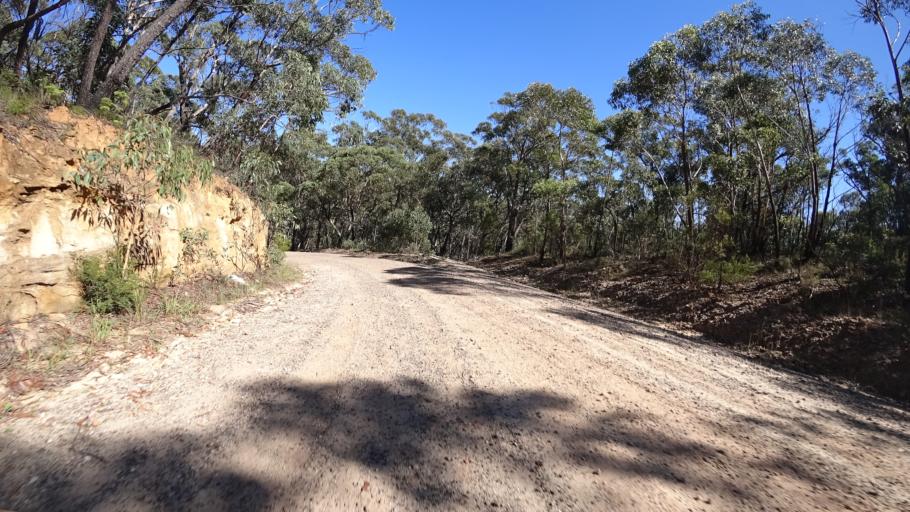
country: AU
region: New South Wales
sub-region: Lithgow
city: Lithgow
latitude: -33.4847
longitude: 150.2604
